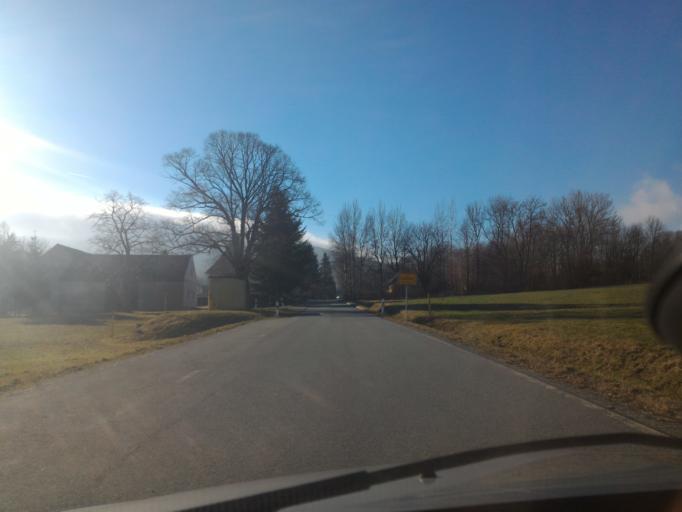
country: DE
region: Saxony
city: Kurort Jonsdorf
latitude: 50.8683
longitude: 14.7253
